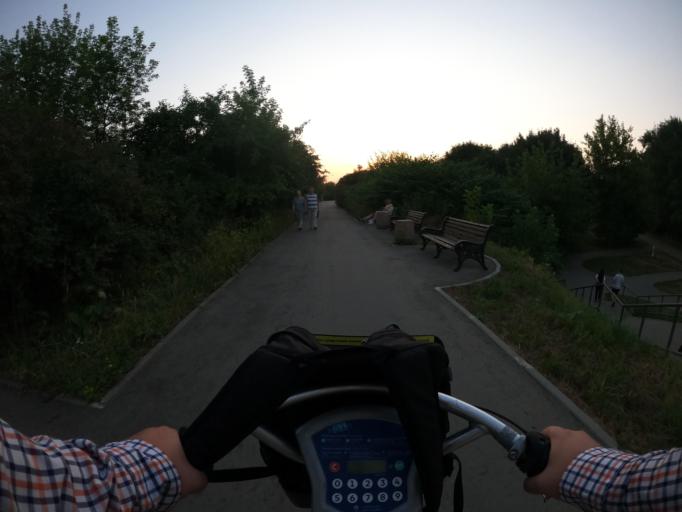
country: RU
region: Moscow
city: Lyublino
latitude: 55.6887
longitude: 37.7612
